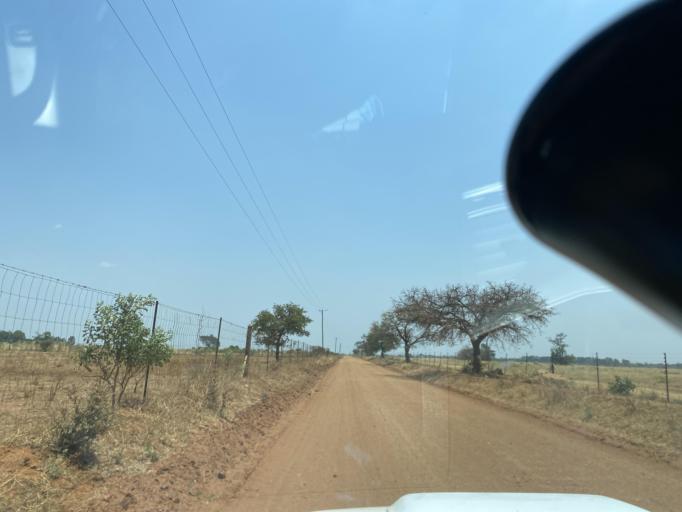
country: ZM
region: Lusaka
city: Lusaka
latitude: -15.4411
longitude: 28.0550
